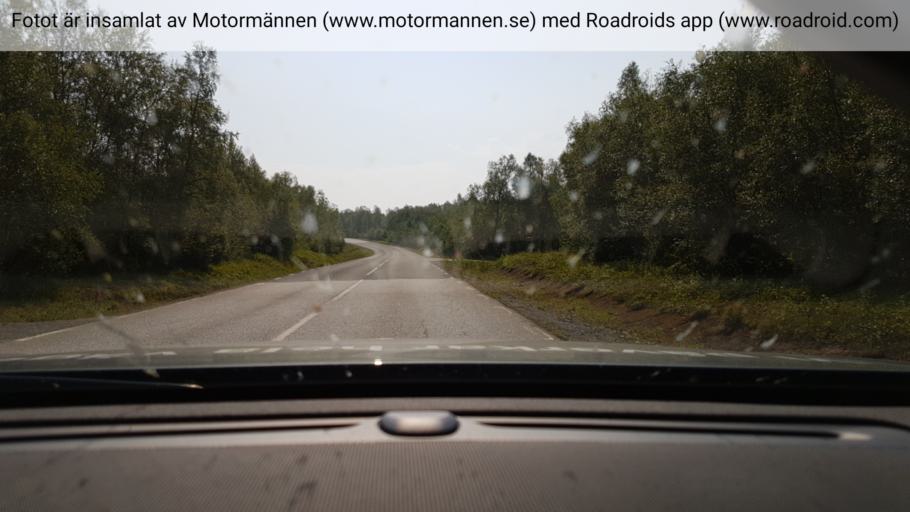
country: NO
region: Nordland
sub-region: Rana
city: Mo i Rana
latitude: 65.7790
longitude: 15.1322
